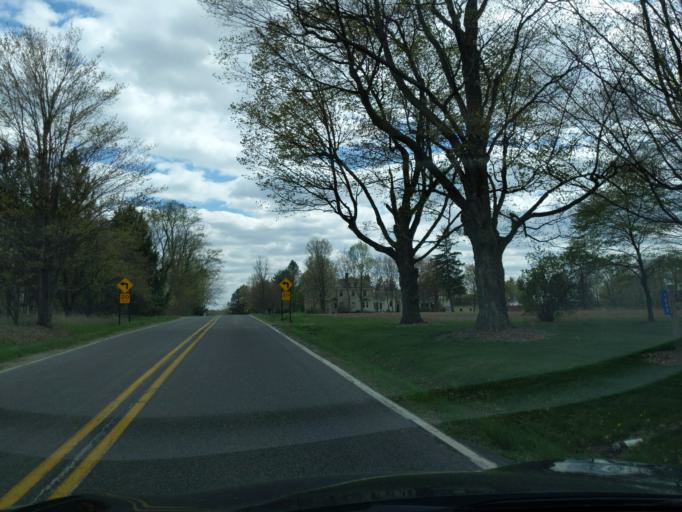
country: US
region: Michigan
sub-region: Ingham County
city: Holt
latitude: 42.6351
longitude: -84.4626
